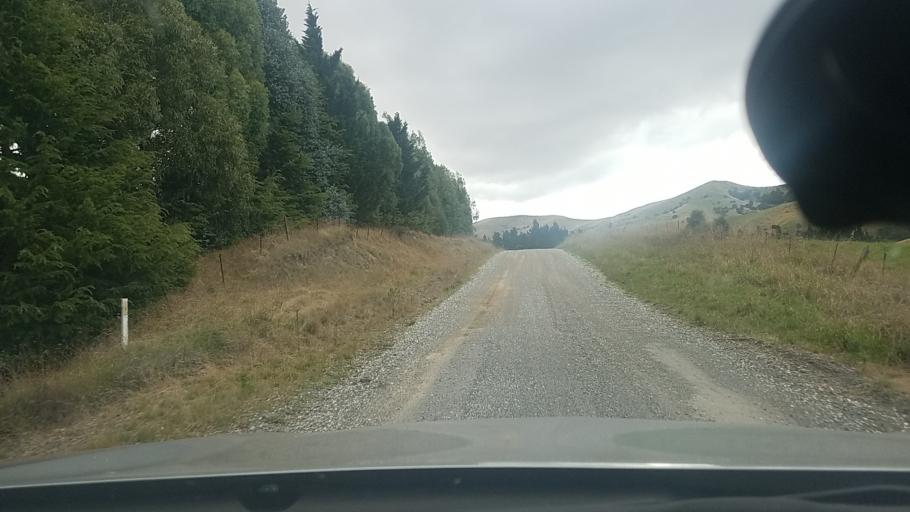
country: NZ
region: Marlborough
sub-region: Marlborough District
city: Blenheim
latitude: -41.5914
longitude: 174.0966
